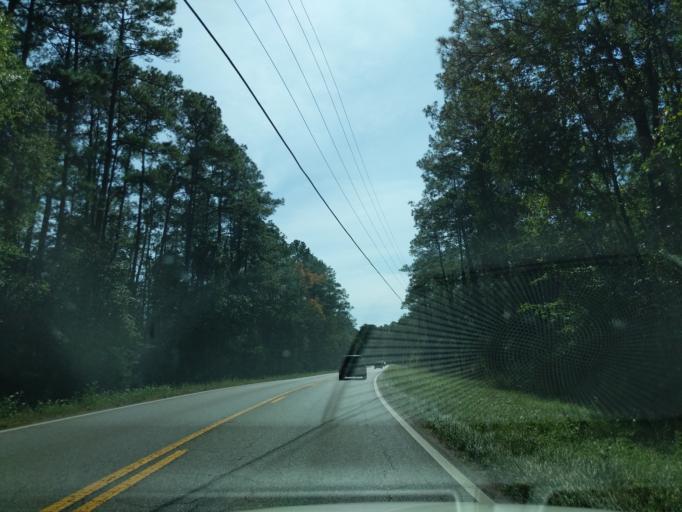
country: US
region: Florida
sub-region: Okaloosa County
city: Crestview
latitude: 30.7435
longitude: -86.6214
